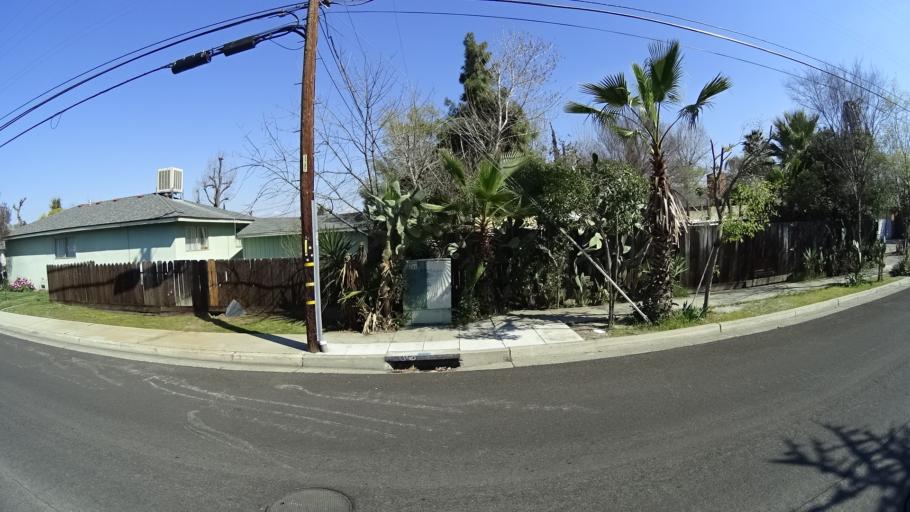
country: US
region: California
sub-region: Fresno County
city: Tarpey Village
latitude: 36.8032
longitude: -119.7318
